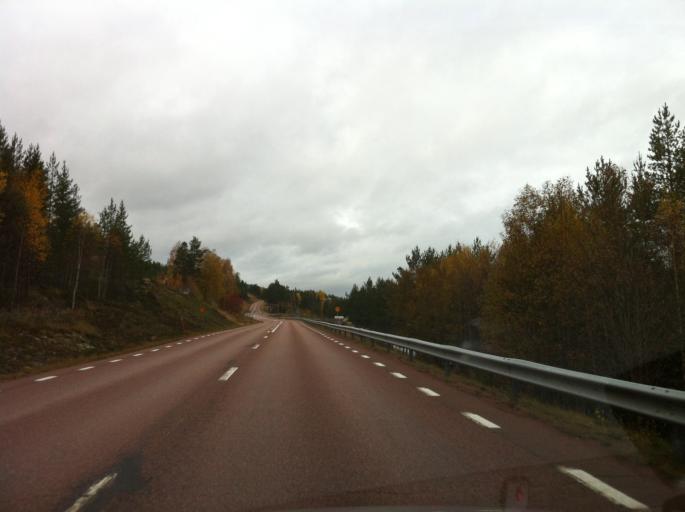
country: SE
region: Dalarna
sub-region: Alvdalens Kommun
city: AElvdalen
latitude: 61.2786
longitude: 13.7705
